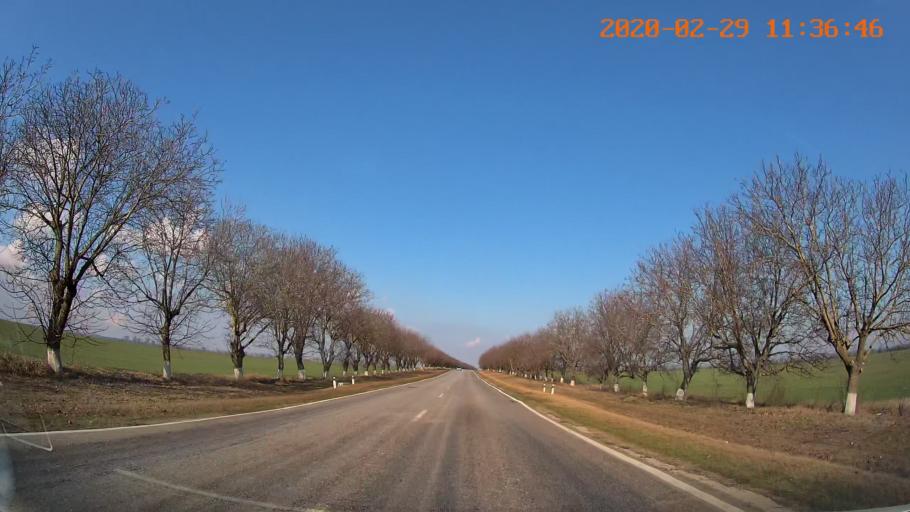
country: MD
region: Rezina
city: Saharna
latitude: 47.6012
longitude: 29.0524
